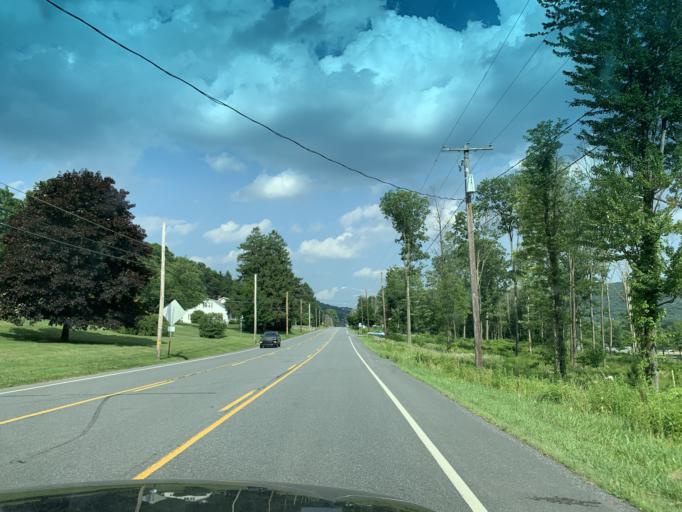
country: US
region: Pennsylvania
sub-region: Schuylkill County
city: Girardville
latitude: 40.7768
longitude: -76.2972
